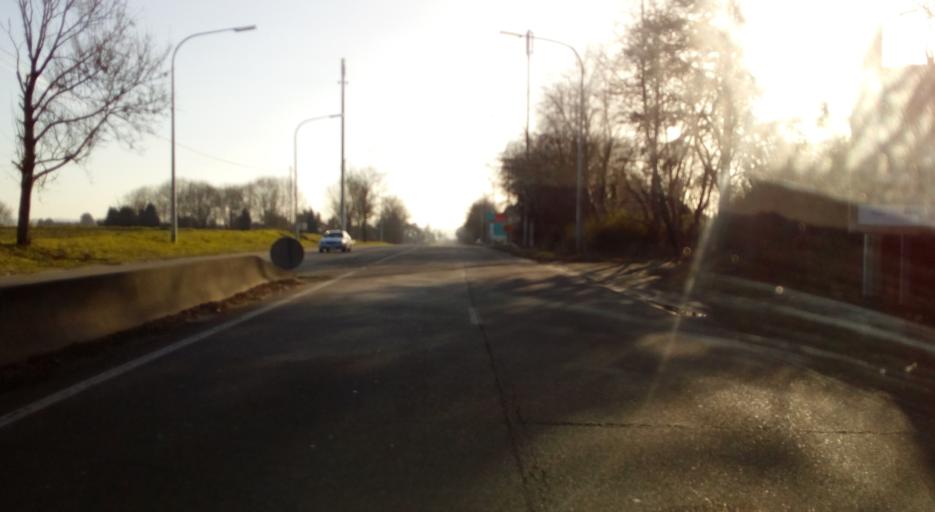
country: BE
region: Wallonia
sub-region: Province du Hainaut
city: Gerpinnes
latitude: 50.3068
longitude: 4.4805
